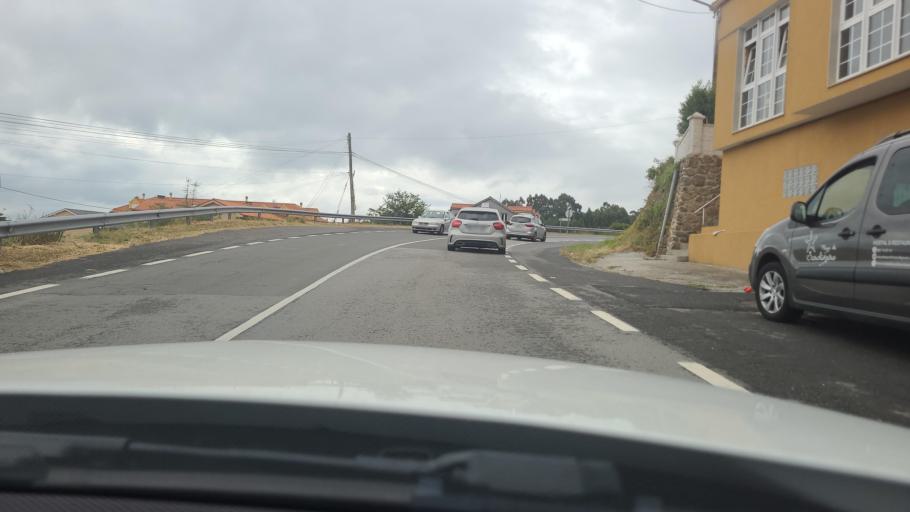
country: ES
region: Galicia
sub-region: Provincia da Coruna
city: Corcubion
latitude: 42.9405
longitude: -9.2351
